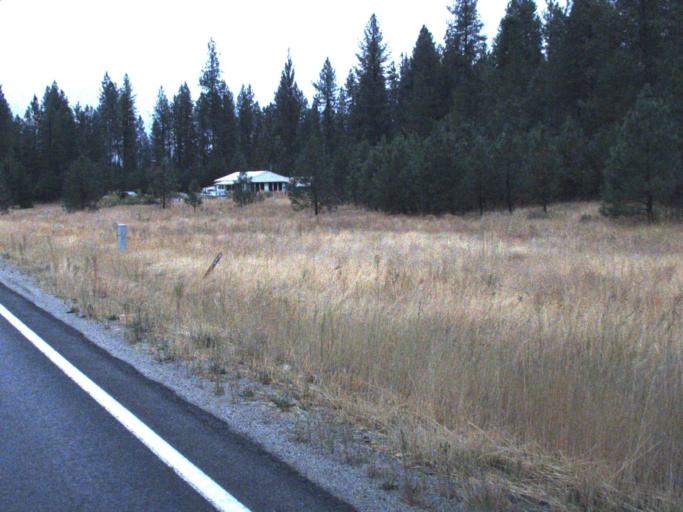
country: US
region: Washington
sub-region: Stevens County
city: Chewelah
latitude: 48.0361
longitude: -117.7349
